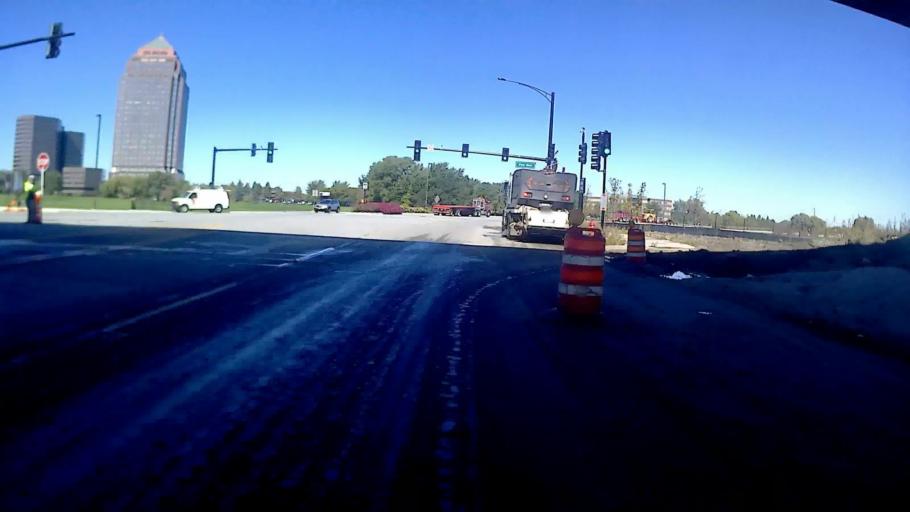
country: US
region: Illinois
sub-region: DuPage County
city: Itasca
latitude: 41.9842
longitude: -88.0125
